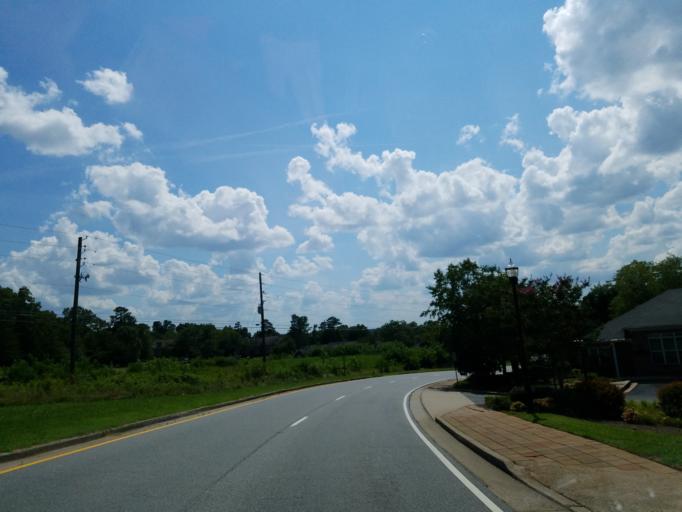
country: US
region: Georgia
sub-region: Forsyth County
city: Cumming
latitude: 34.2067
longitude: -84.1310
